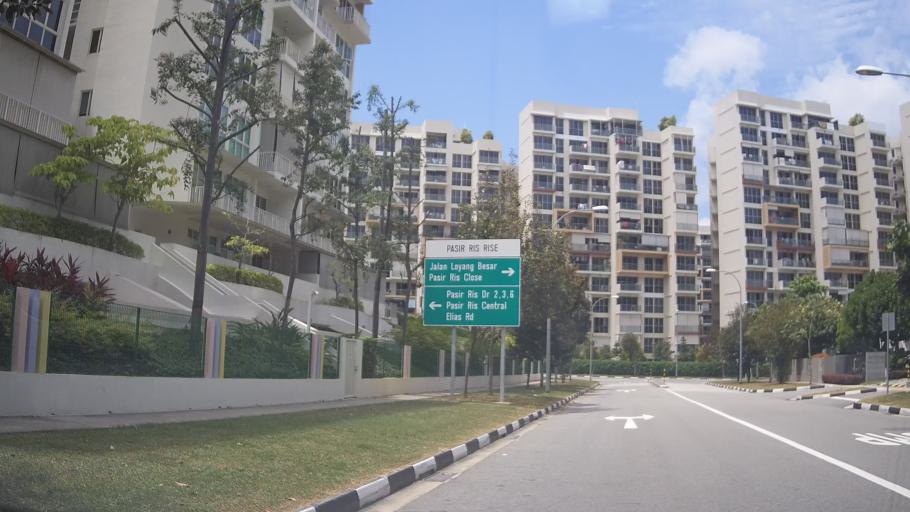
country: MY
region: Johor
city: Kampung Pasir Gudang Baru
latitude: 1.3770
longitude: 103.9602
